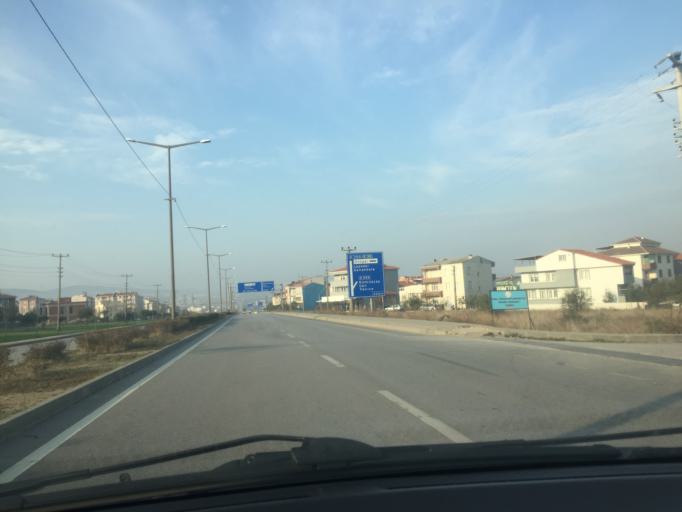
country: TR
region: Canakkale
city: Biga
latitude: 40.2430
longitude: 27.2671
